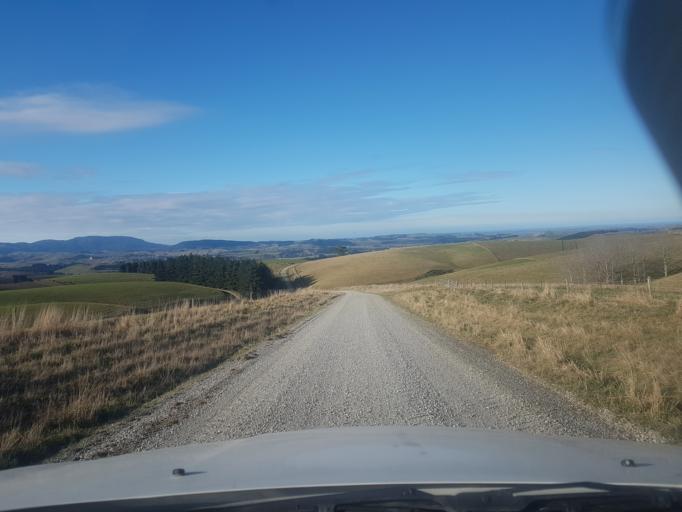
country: NZ
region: Canterbury
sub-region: Timaru District
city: Pleasant Point
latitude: -44.1675
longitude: 170.9077
